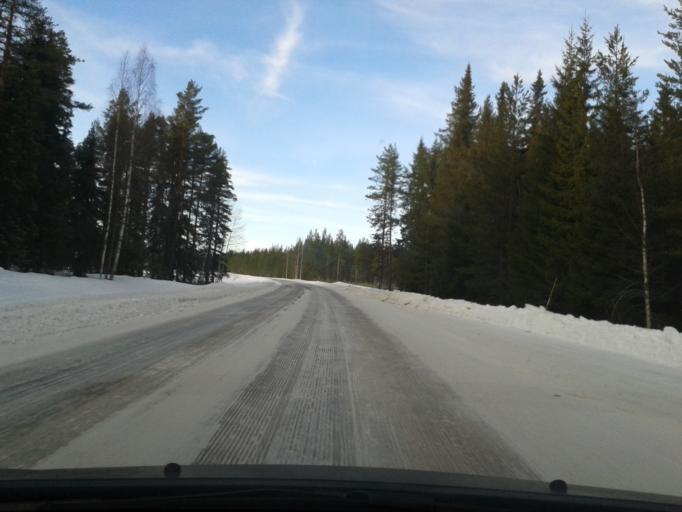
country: SE
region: Vaesternorrland
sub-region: OErnskoeldsviks Kommun
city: Bredbyn
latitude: 63.5937
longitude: 17.9192
